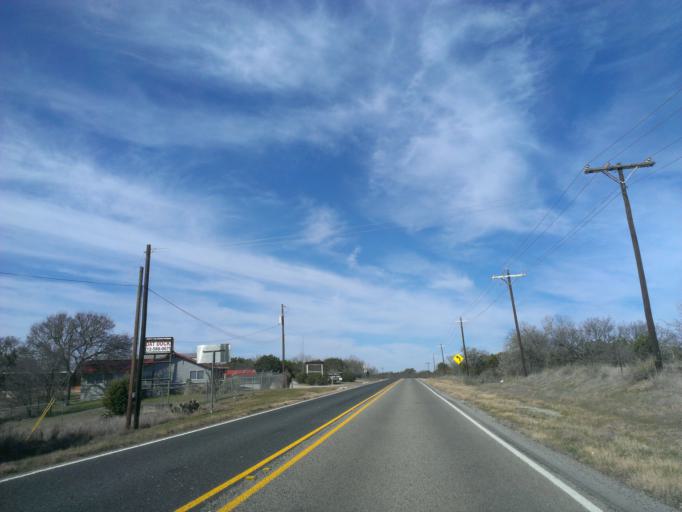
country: US
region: Texas
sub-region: Burnet County
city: Granite Shoals
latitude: 30.5944
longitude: -98.4281
